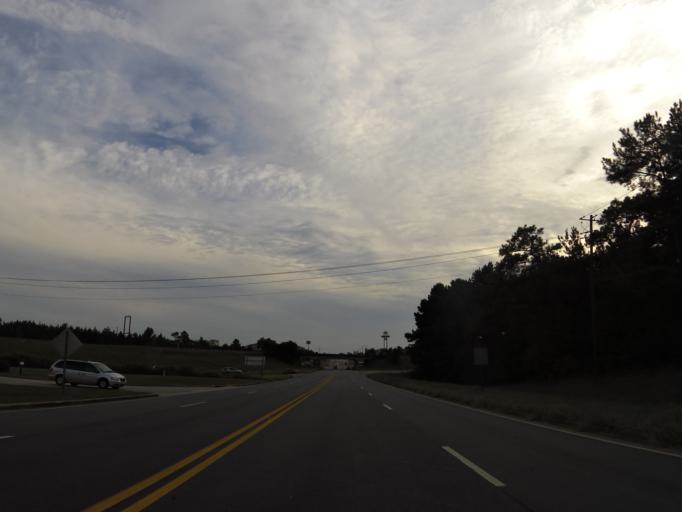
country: US
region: Alabama
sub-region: Escambia County
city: Atmore
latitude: 31.1127
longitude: -87.4728
